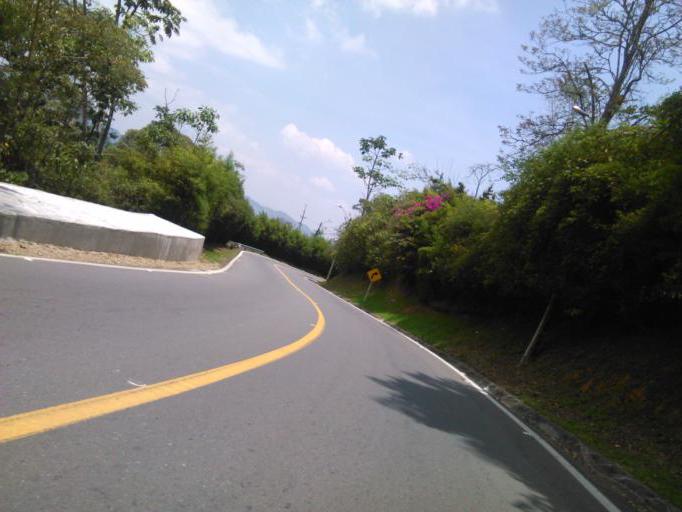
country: CO
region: Antioquia
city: La Ceja
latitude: 6.0095
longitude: -75.4072
